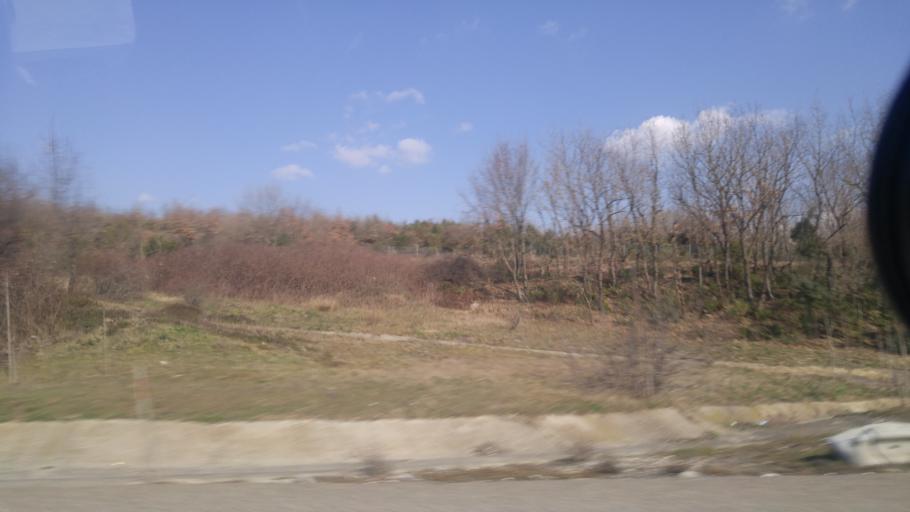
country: TR
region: Istanbul
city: Canta
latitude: 41.1831
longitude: 28.1110
